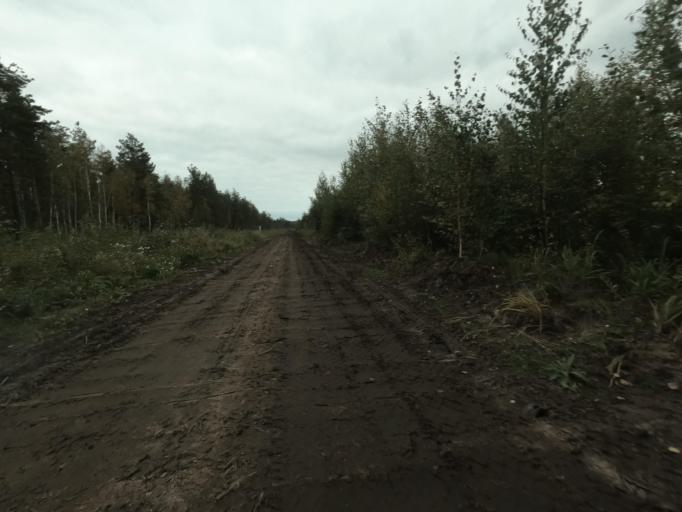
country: RU
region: St.-Petersburg
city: Sapernyy
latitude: 59.7623
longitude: 30.7207
